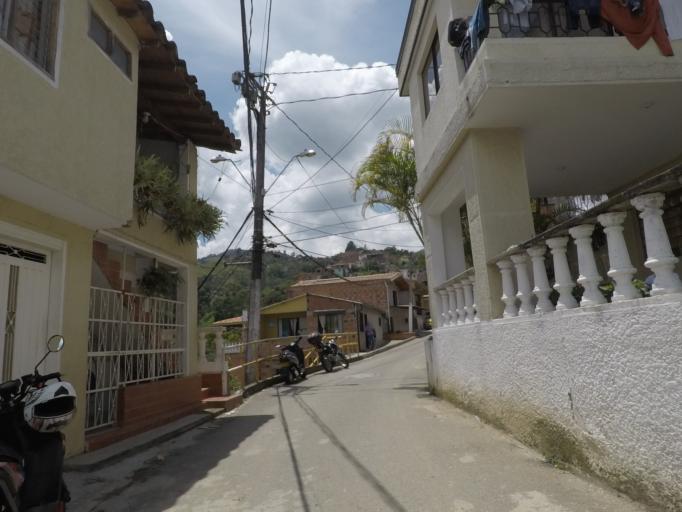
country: CO
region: Antioquia
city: Medellin
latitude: 6.2741
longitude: -75.6318
